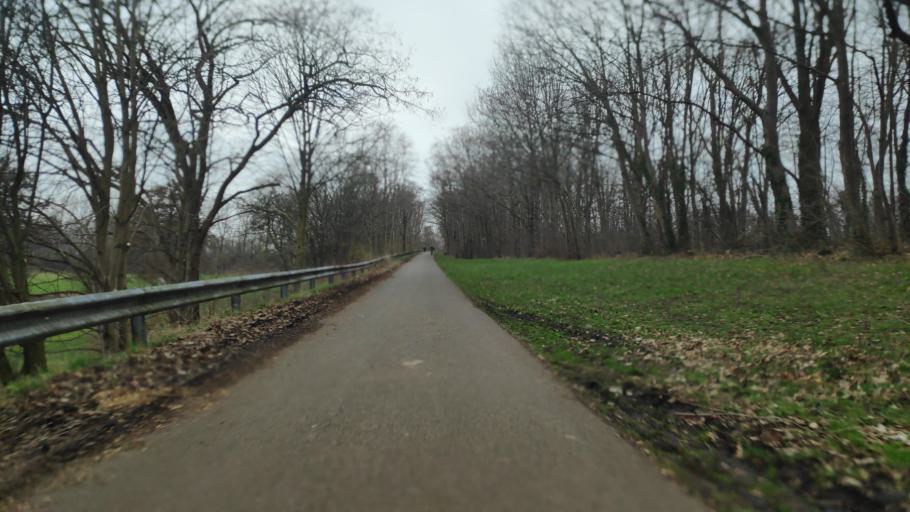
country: DE
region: North Rhine-Westphalia
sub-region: Regierungsbezirk Detmold
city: Minden
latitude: 52.2977
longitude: 8.8552
